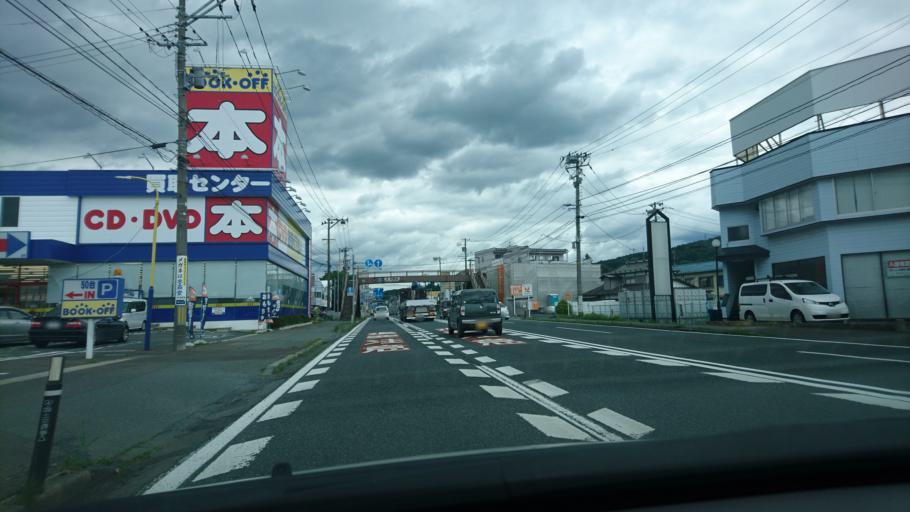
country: JP
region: Iwate
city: Morioka-shi
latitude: 39.6909
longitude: 141.1658
